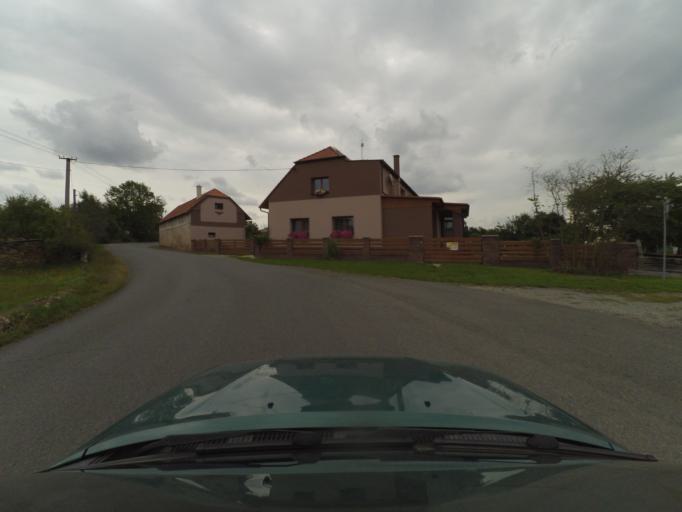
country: CZ
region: Plzensky
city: Kralovice
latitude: 49.9186
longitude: 13.5190
